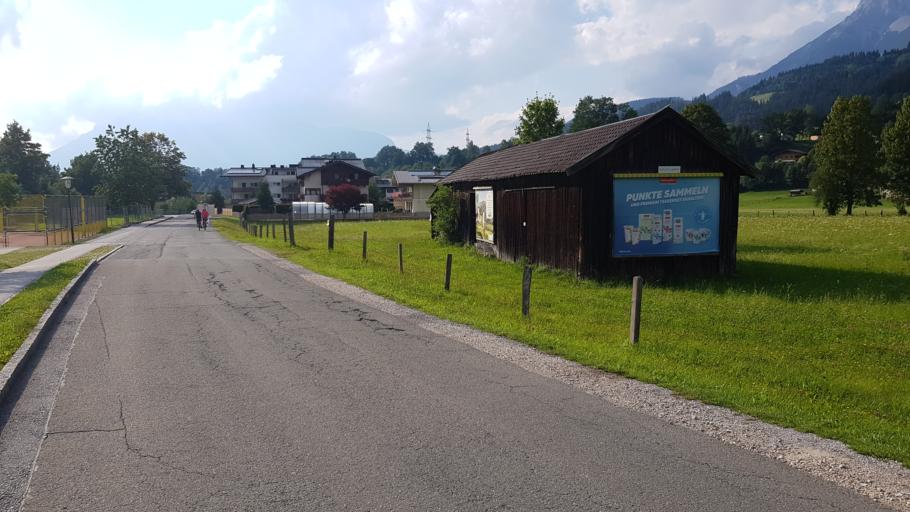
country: AT
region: Salzburg
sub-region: Politischer Bezirk Zell am See
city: Maria Alm am Steinernen Meer
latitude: 47.4067
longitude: 12.8976
